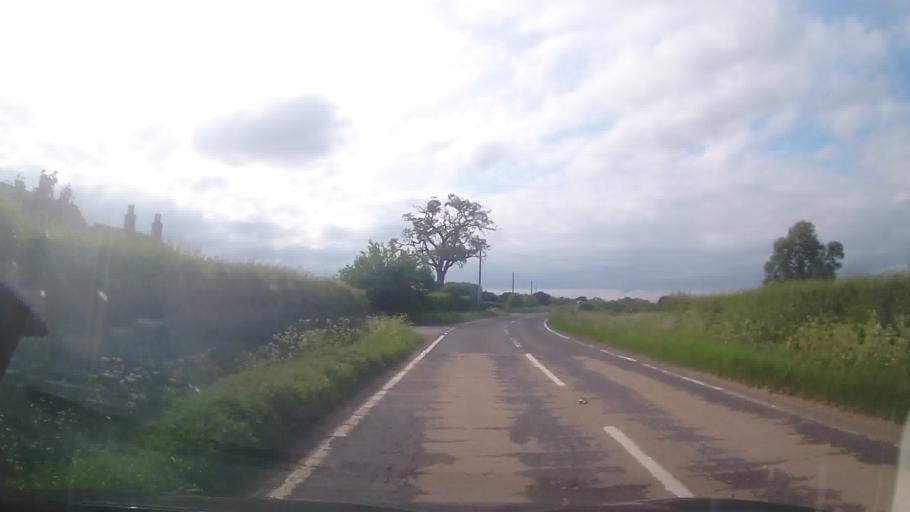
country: GB
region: England
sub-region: Shropshire
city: Petton
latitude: 52.8192
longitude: -2.7943
